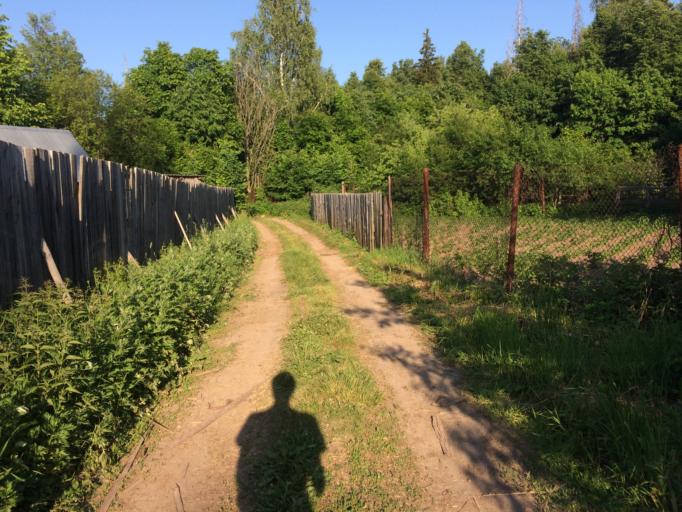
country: RU
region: Mariy-El
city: Mochalishche
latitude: 56.5425
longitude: 48.4097
